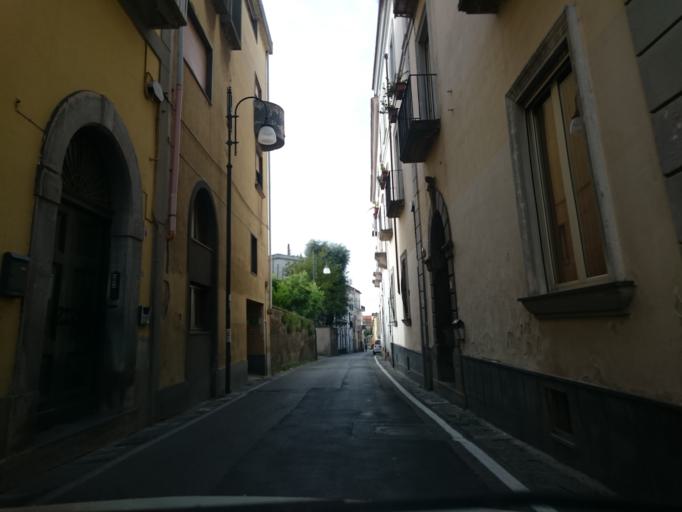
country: IT
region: Campania
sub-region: Provincia di Napoli
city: Sant'Agnello
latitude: 40.6327
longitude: 14.4014
